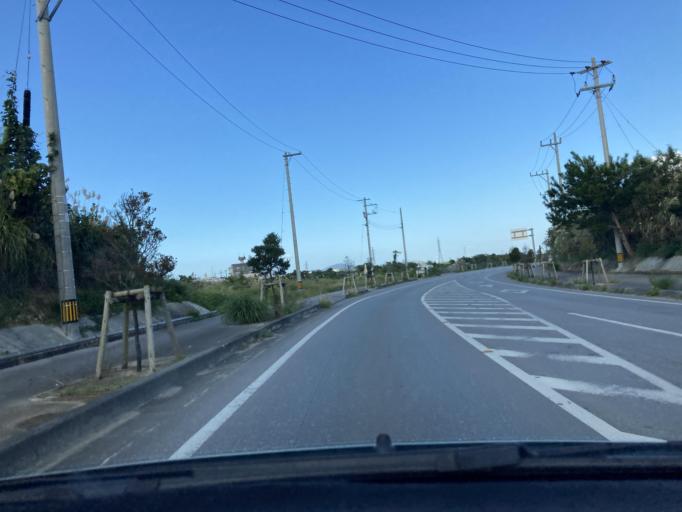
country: JP
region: Okinawa
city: Gushikawa
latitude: 26.3737
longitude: 127.8272
